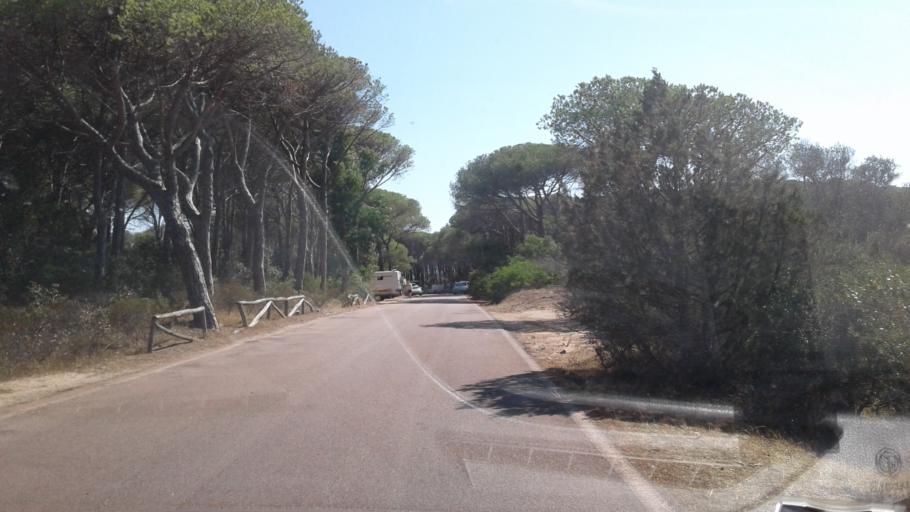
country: IT
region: Sardinia
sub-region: Provincia di Olbia-Tempio
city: La Maddalena
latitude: 41.2085
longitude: 9.4612
